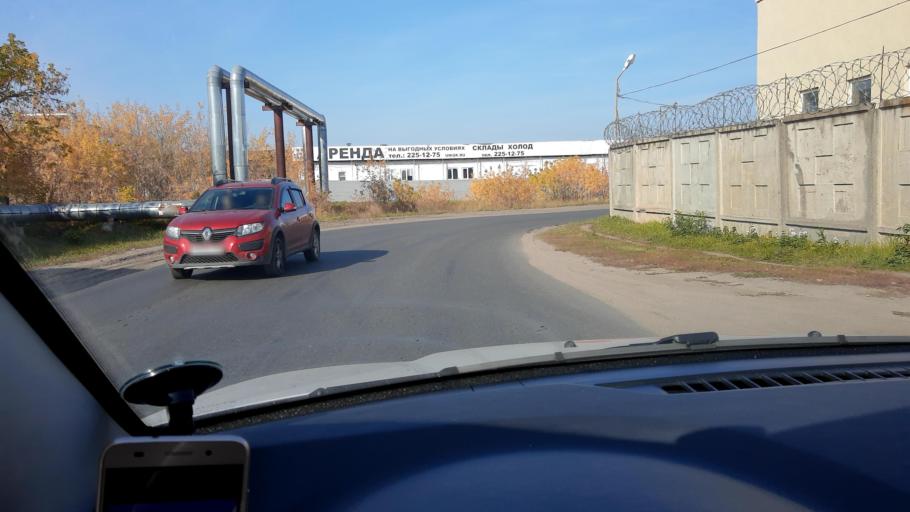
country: RU
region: Nizjnij Novgorod
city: Gorbatovka
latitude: 56.3442
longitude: 43.8220
